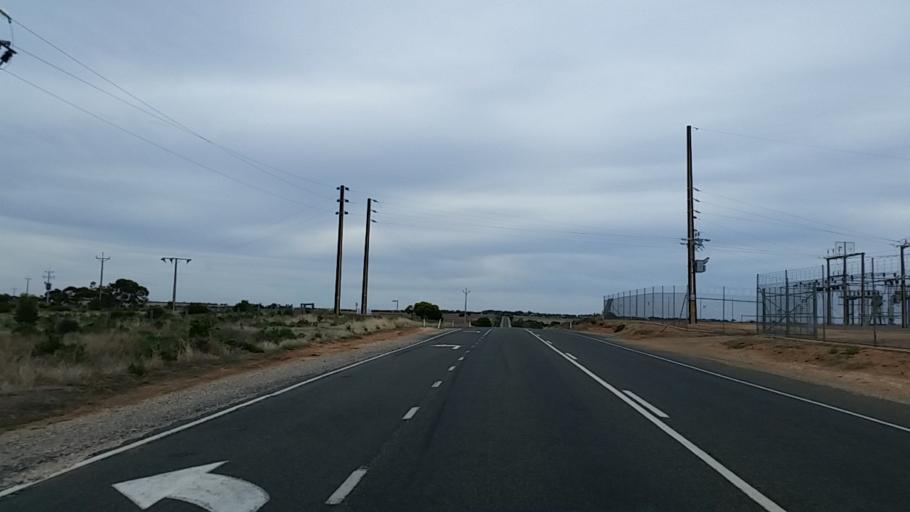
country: AU
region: South Australia
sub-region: Mid Murray
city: Mannum
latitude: -34.9168
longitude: 139.2637
